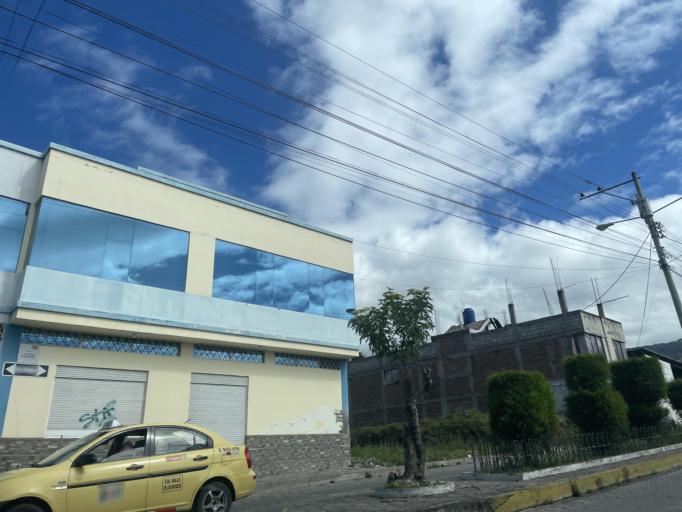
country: EC
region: Chimborazo
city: Guano
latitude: -1.6050
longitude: -78.6427
